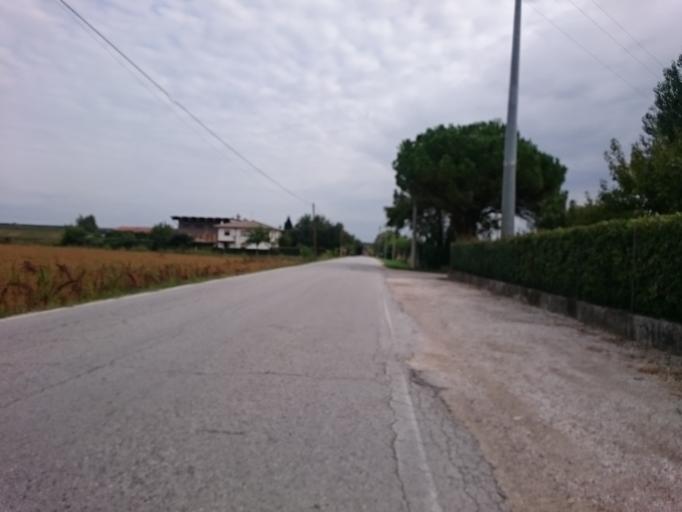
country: IT
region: Veneto
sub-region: Provincia di Vicenza
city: Grisignano di Zocco
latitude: 45.4826
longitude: 11.6858
